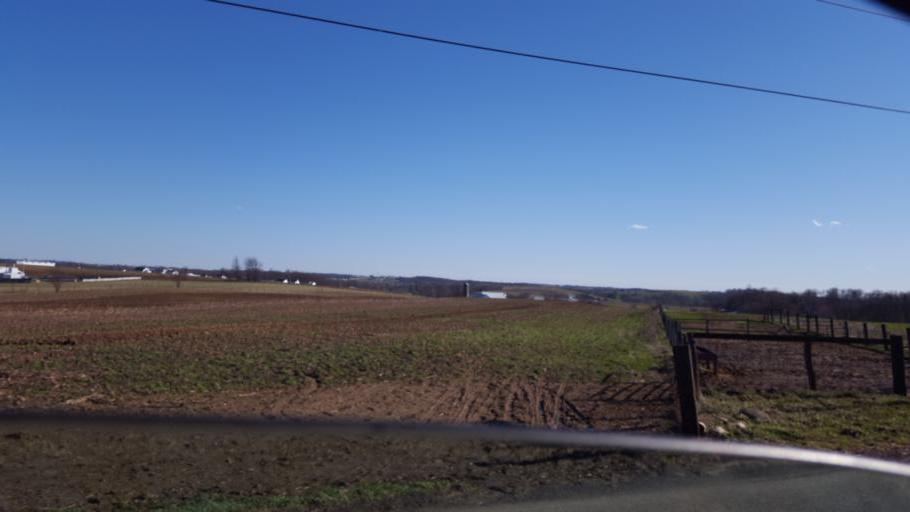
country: US
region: Ohio
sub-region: Wayne County
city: Apple Creek
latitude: 40.6493
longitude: -81.7712
